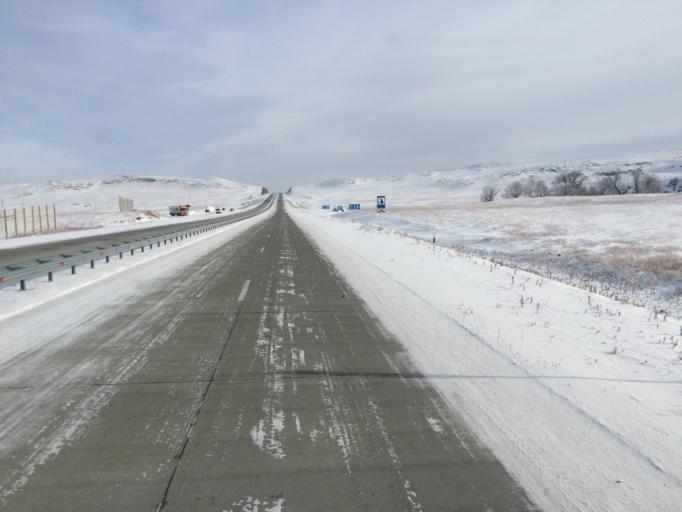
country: KZ
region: Zhambyl
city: Georgiyevka
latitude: 43.4335
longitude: 74.9317
